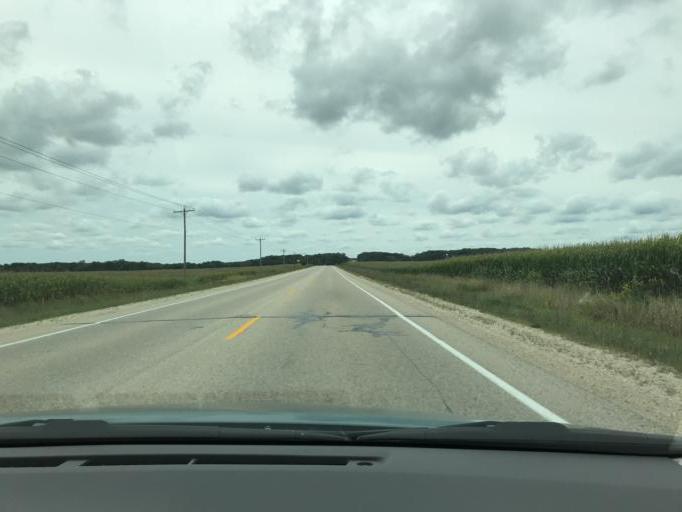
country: US
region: Wisconsin
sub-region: Racine County
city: Bohners Lake
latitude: 42.6175
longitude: -88.2353
